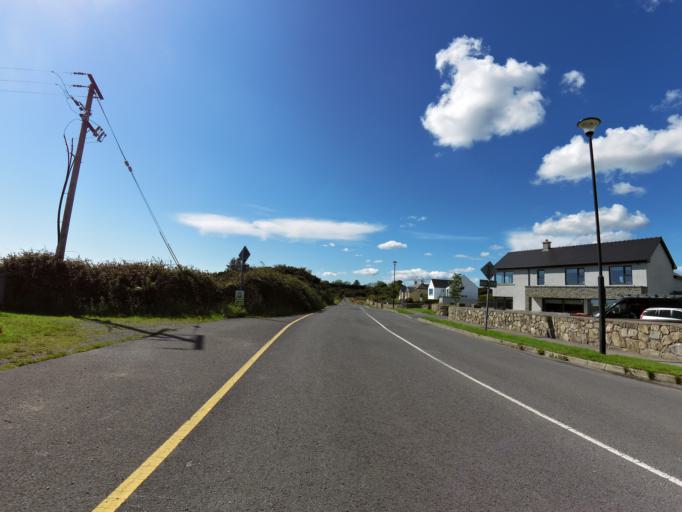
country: IE
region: Connaught
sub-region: County Galway
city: Gaillimh
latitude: 53.2843
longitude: -9.0858
